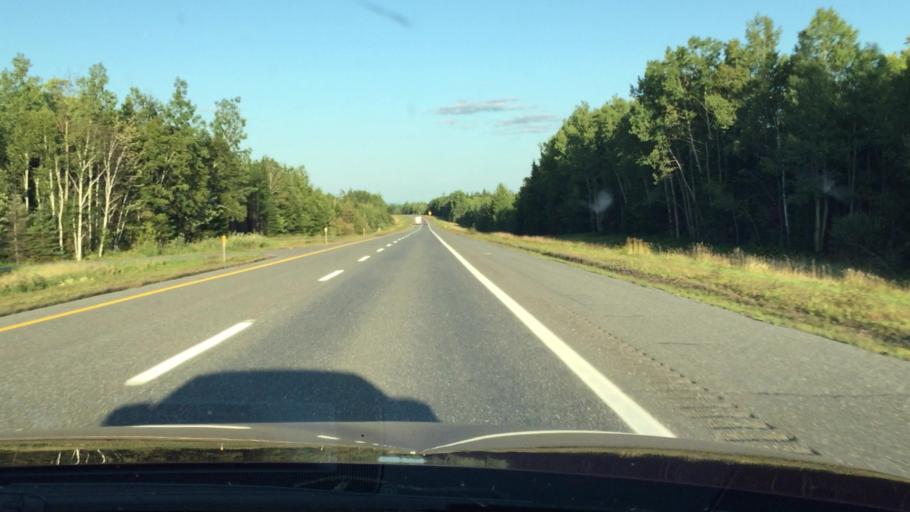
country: US
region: Maine
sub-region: Aroostook County
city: Hodgdon
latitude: 46.1419
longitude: -68.0338
